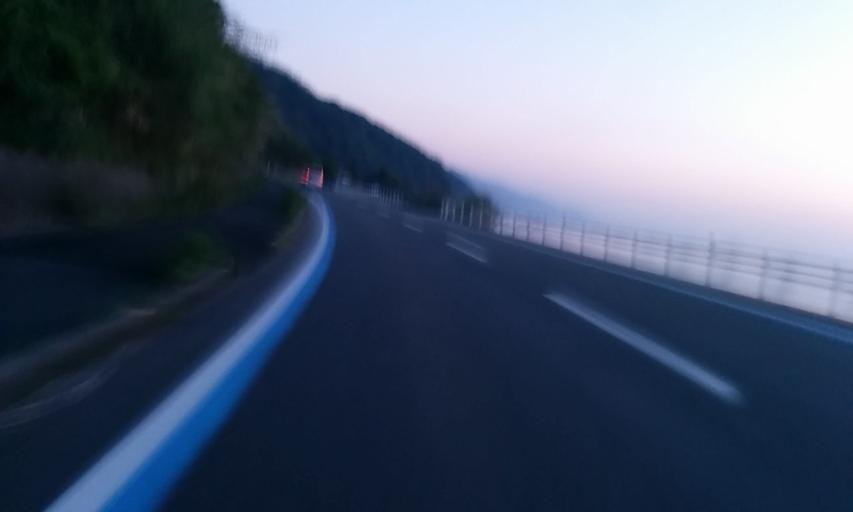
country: JP
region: Ehime
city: Ozu
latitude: 33.5828
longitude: 132.4485
